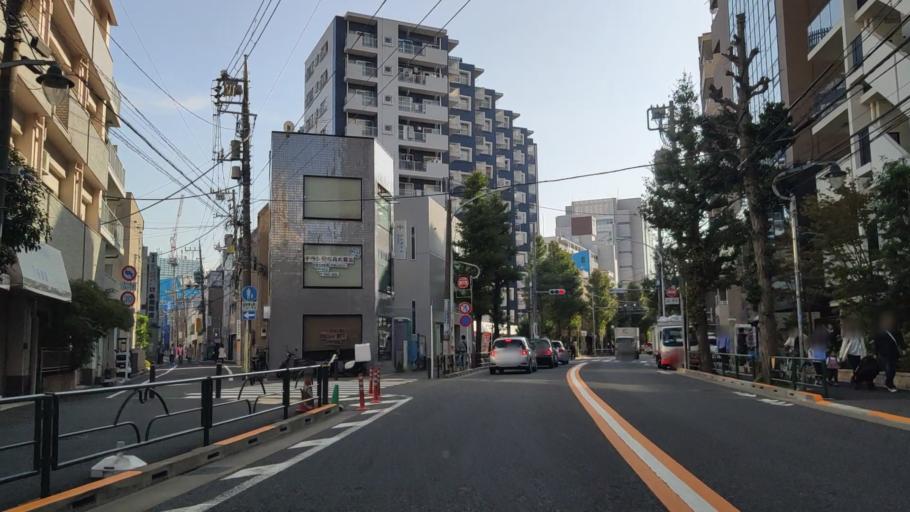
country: JP
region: Tokyo
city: Tokyo
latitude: 35.6997
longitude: 139.6675
